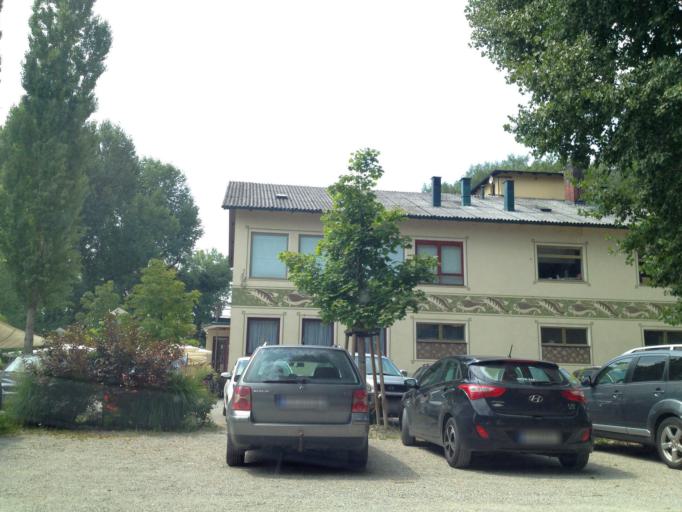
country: AT
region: Lower Austria
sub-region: Politischer Bezirk Ganserndorf
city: Orth an der Donau
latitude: 48.1245
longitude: 16.7126
